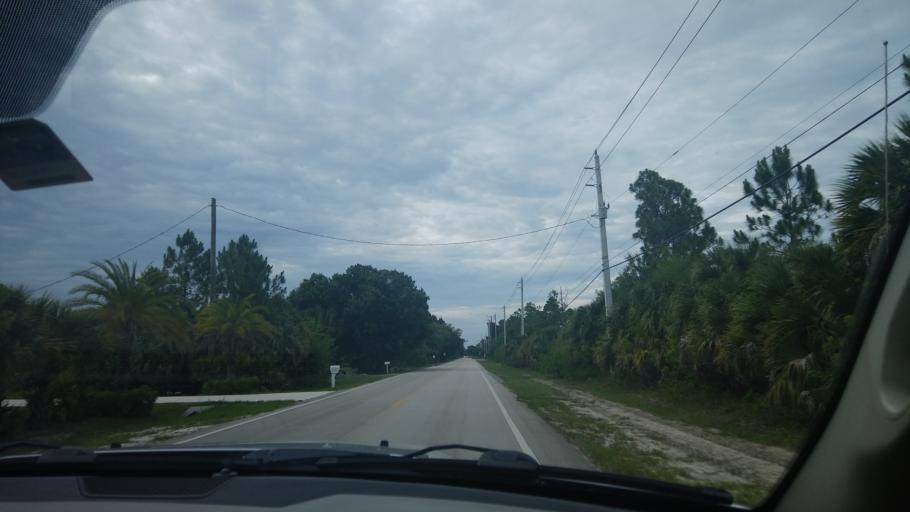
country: US
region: Florida
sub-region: Indian River County
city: Fellsmere
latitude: 27.7514
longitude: -80.5933
